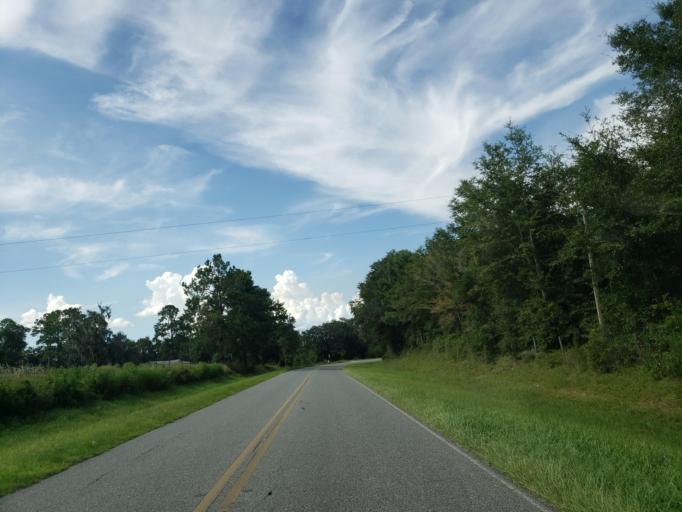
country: US
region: Georgia
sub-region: Echols County
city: Statenville
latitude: 30.6131
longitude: -83.2178
